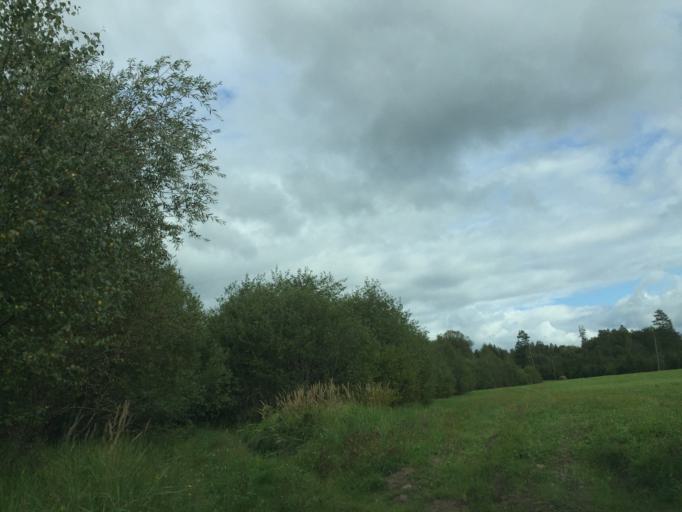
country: LV
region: Pargaujas
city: Stalbe
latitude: 57.4983
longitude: 24.9149
